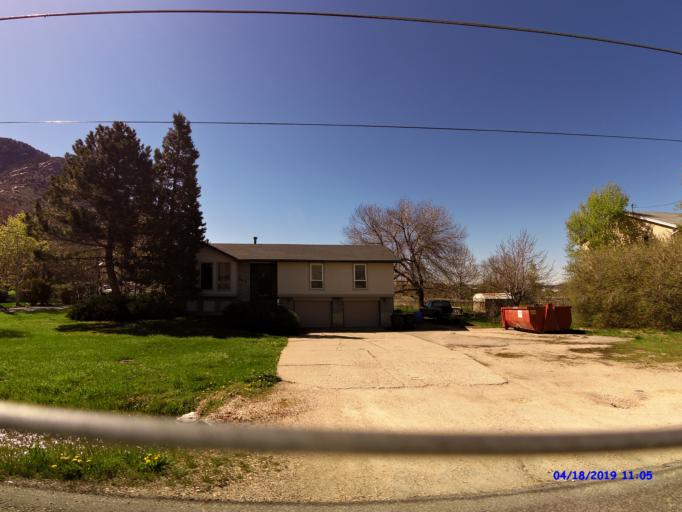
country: US
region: Utah
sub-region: Weber County
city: North Ogden
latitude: 41.2889
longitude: -111.9517
